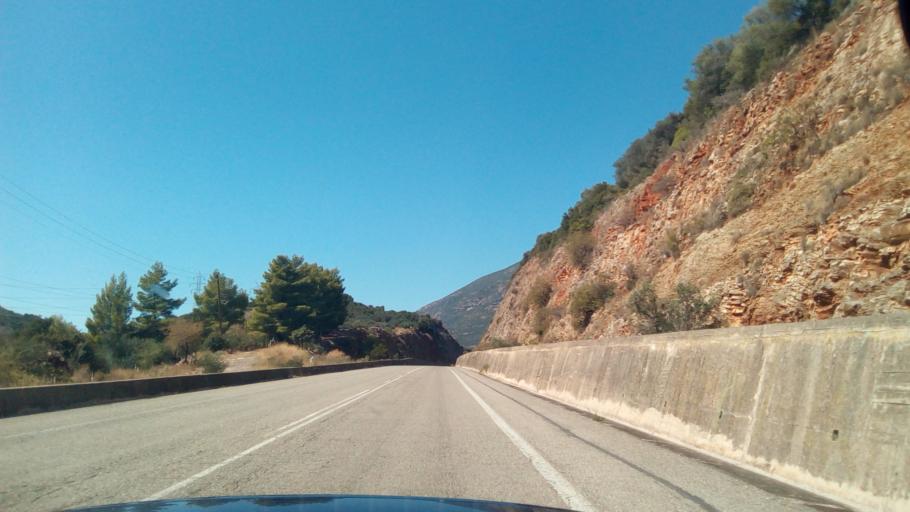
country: GR
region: West Greece
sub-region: Nomos Achaias
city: Selianitika
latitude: 38.3876
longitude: 22.0804
